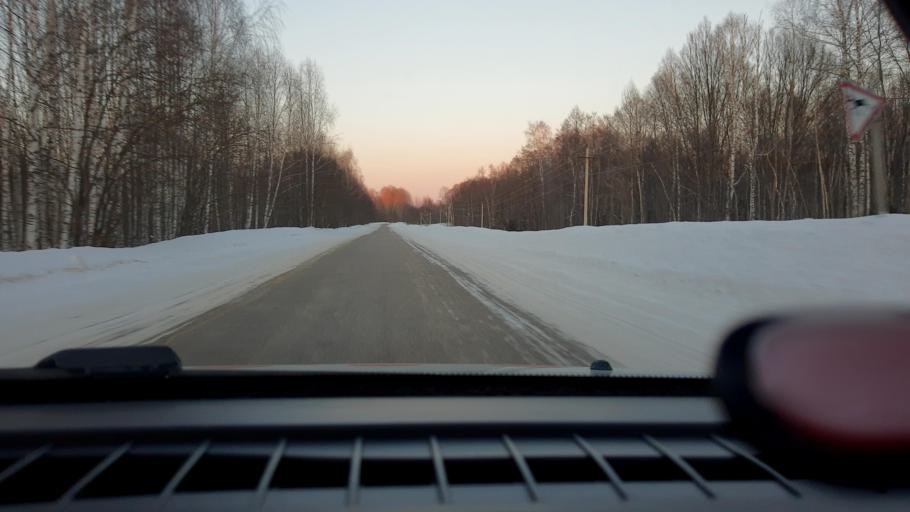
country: RU
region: Nizjnij Novgorod
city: Lyskovo
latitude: 56.1588
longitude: 45.1630
